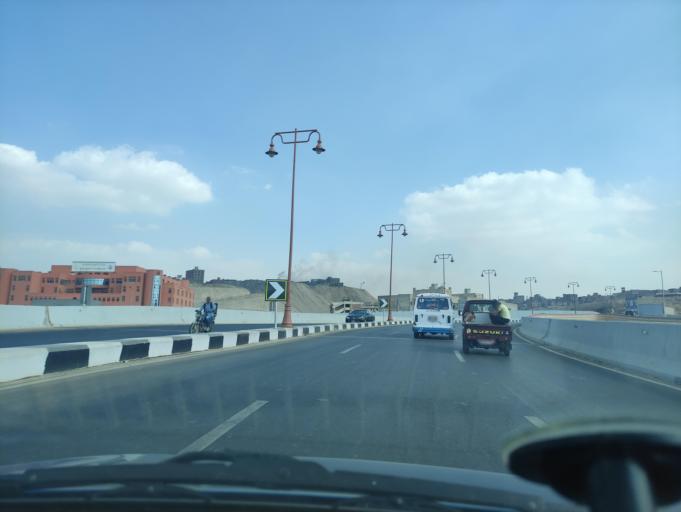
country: EG
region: Muhafazat al Qahirah
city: Cairo
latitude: 30.0500
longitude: 31.2861
